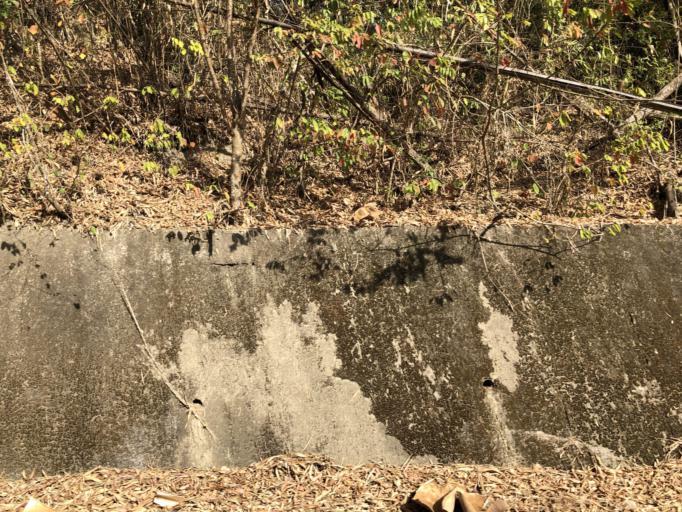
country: TW
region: Taiwan
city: Yujing
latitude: 23.0211
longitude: 120.3974
